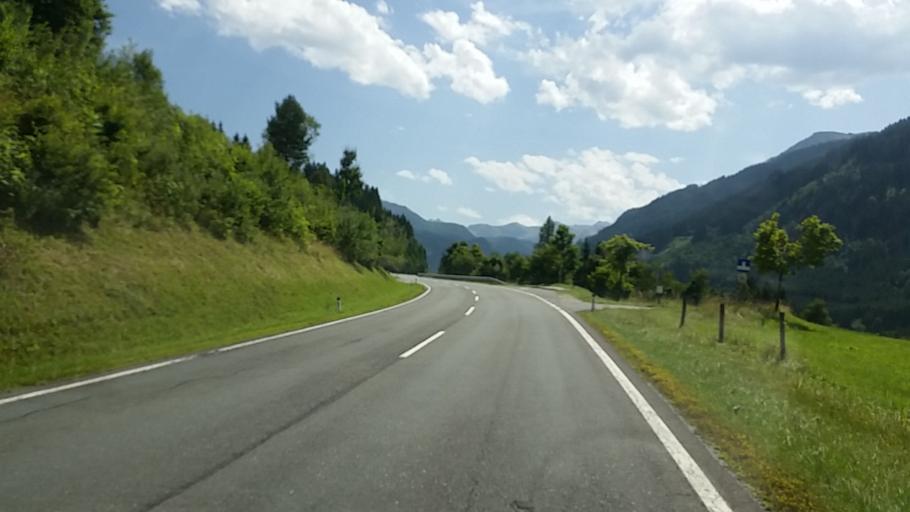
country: AT
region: Salzburg
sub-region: Politischer Bezirk Sankt Johann im Pongau
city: Forstau
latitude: 47.3494
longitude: 13.5015
